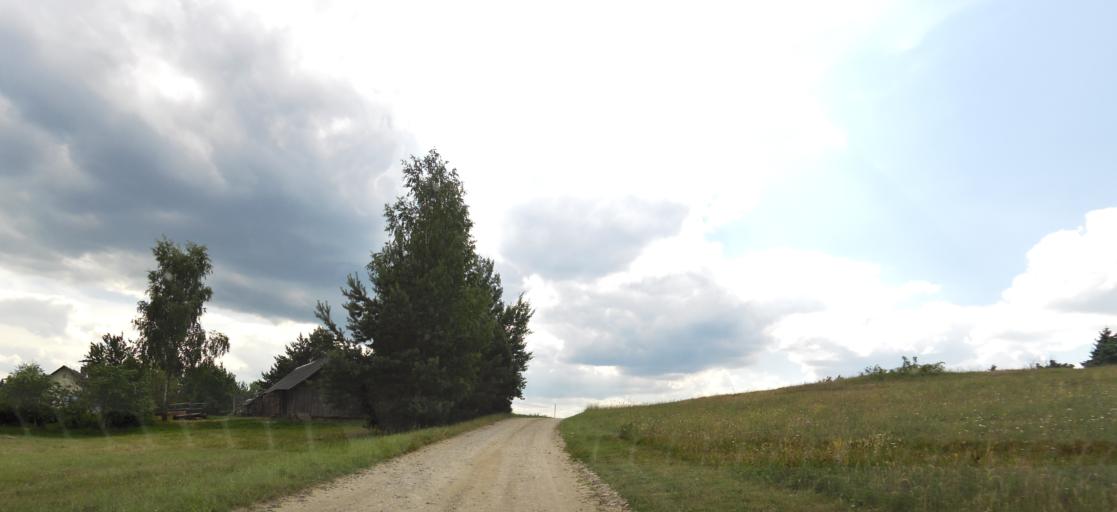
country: LT
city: Skaidiskes
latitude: 54.5310
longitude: 25.6286
